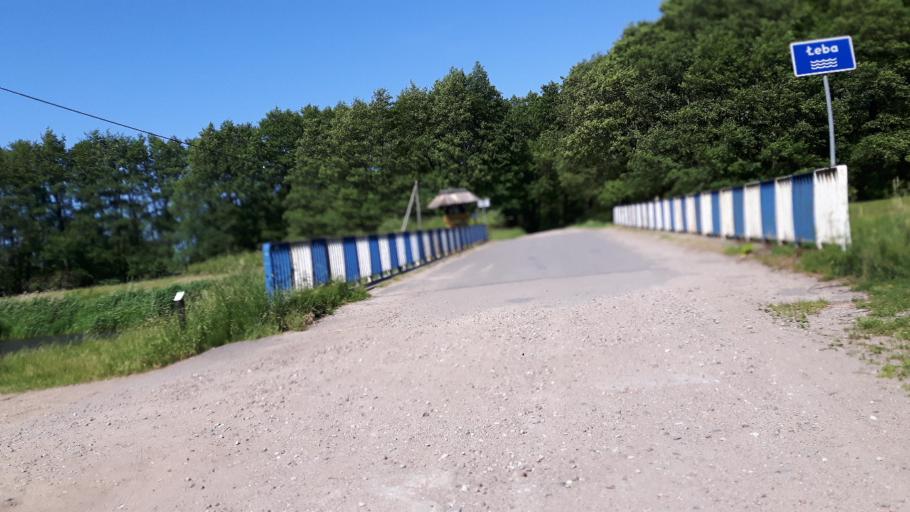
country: PL
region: Pomeranian Voivodeship
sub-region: Powiat slupski
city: Glowczyce
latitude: 54.6922
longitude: 17.4483
